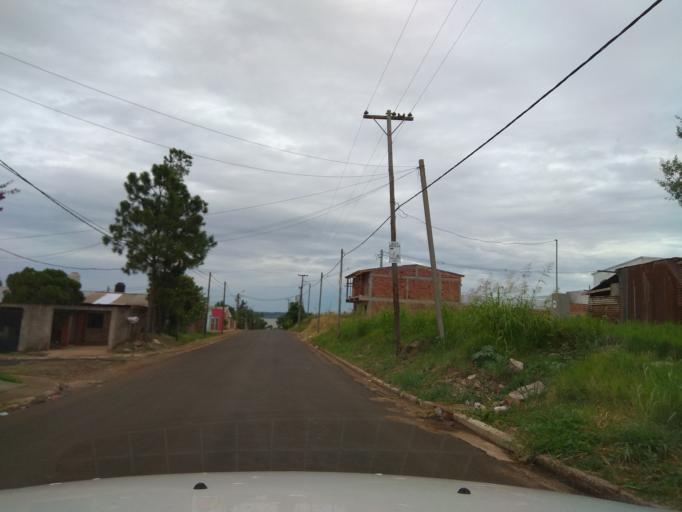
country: AR
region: Misiones
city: Garupa
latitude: -27.4488
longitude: -55.8551
